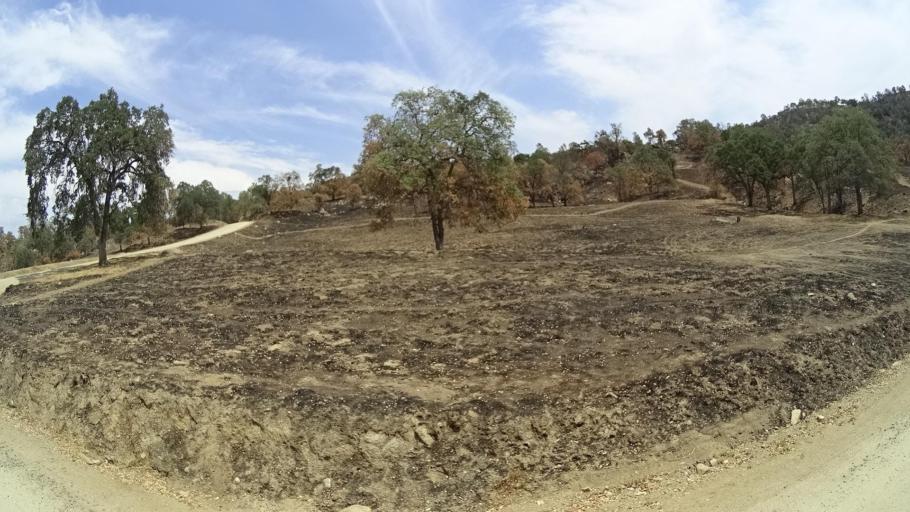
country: US
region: California
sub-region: Madera County
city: Ahwahnee
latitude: 37.3507
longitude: -119.8697
